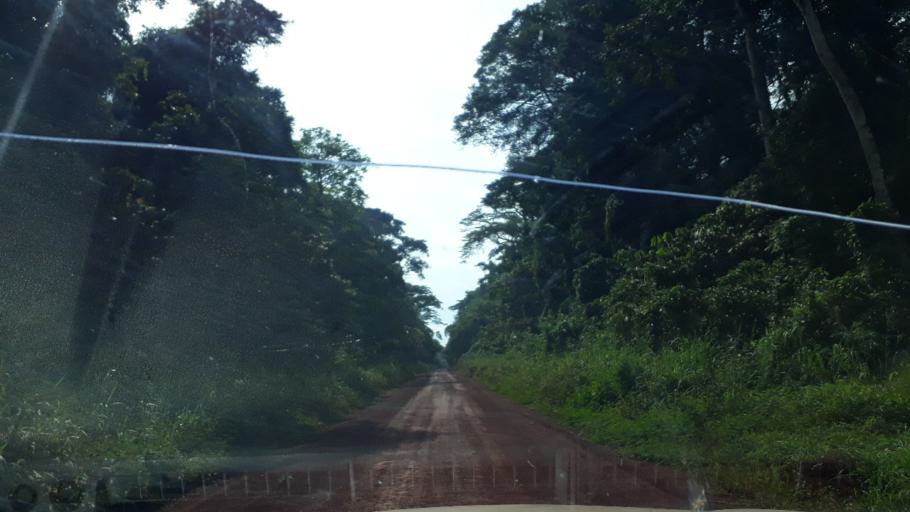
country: CD
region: Eastern Province
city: Wamba
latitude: 1.4167
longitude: 27.8057
